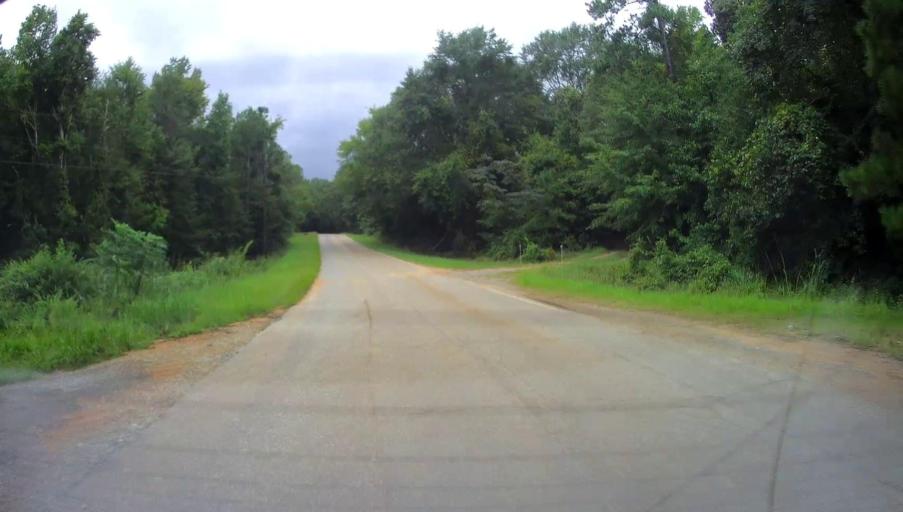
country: US
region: Georgia
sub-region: Bibb County
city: Macon
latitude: 32.7739
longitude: -83.5088
